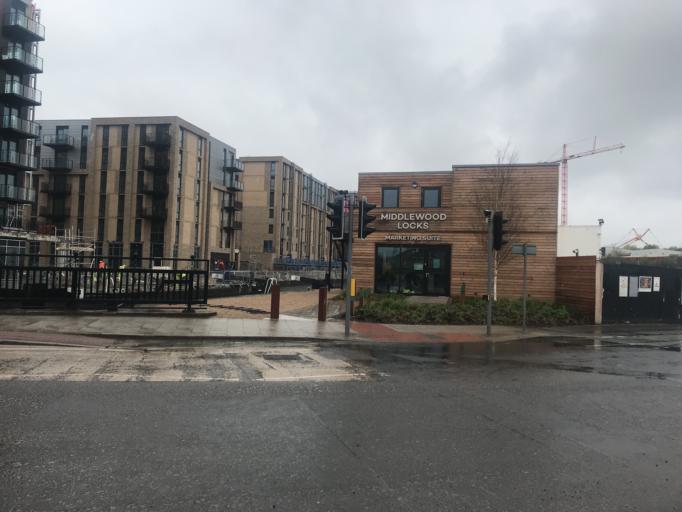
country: GB
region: England
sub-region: Manchester
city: Hulme
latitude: 53.4796
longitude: -2.2620
